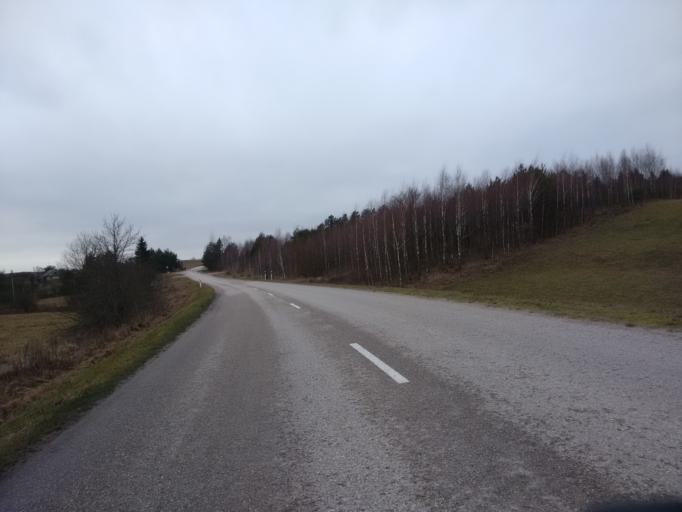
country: LT
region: Alytaus apskritis
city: Druskininkai
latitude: 54.2200
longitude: 23.9123
